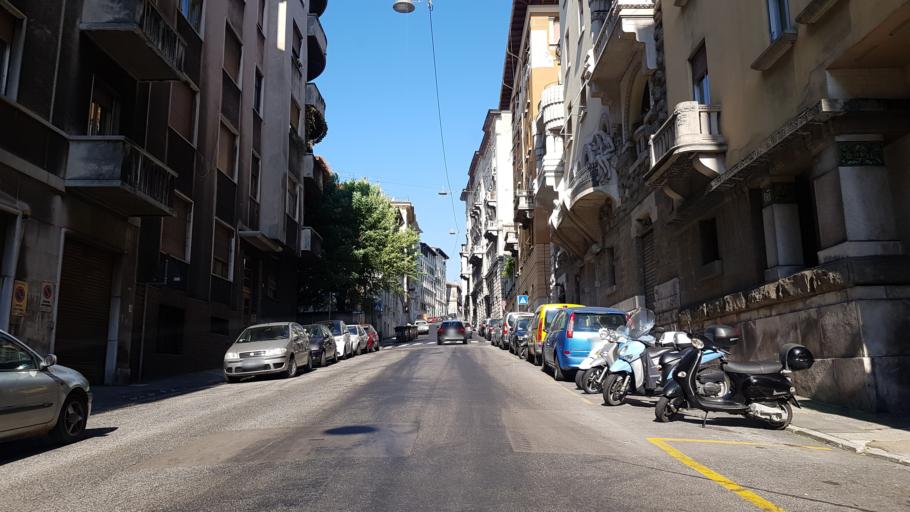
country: IT
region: Friuli Venezia Giulia
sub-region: Provincia di Trieste
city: Trieste
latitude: 45.6580
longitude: 13.7762
